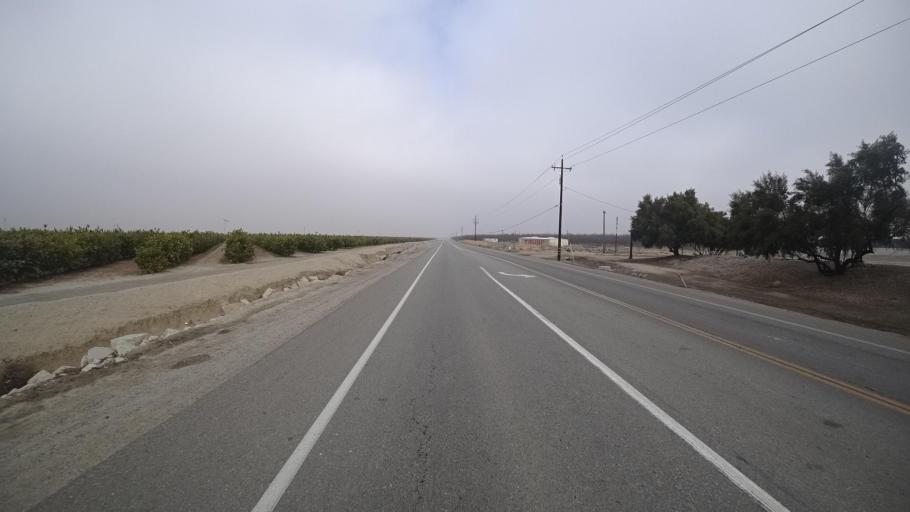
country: US
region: California
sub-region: Kern County
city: Pine Mountain Club
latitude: 35.0696
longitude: -119.1313
